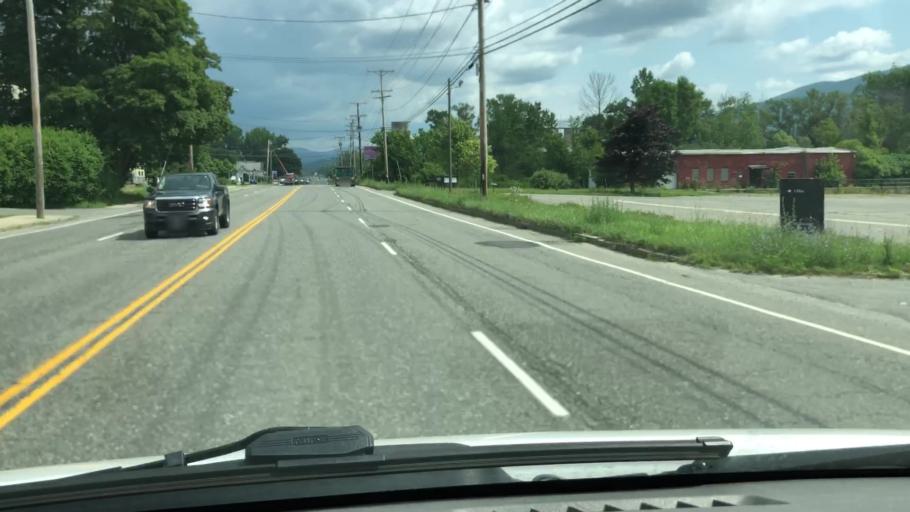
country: US
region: Massachusetts
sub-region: Berkshire County
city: Adams
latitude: 42.6511
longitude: -73.1109
